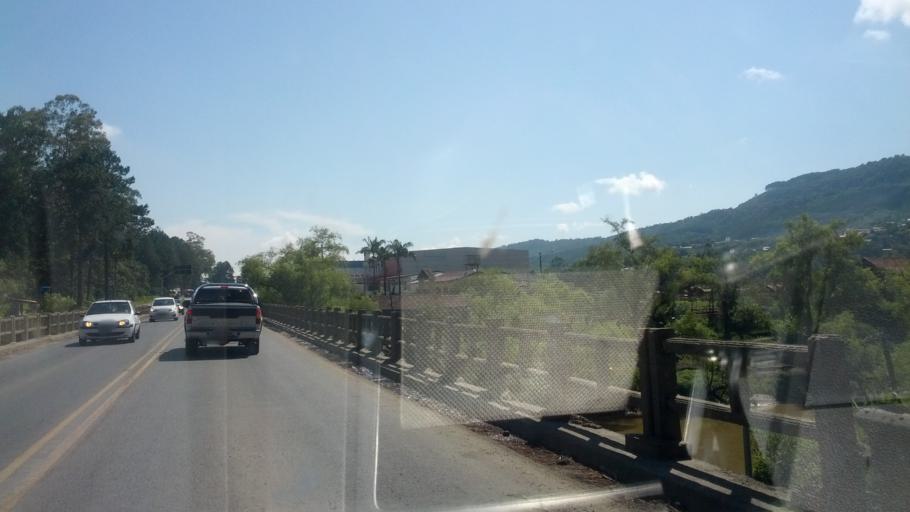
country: BR
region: Santa Catarina
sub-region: Rio Do Sul
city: Rio do Sul
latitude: -27.2446
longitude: -49.6919
